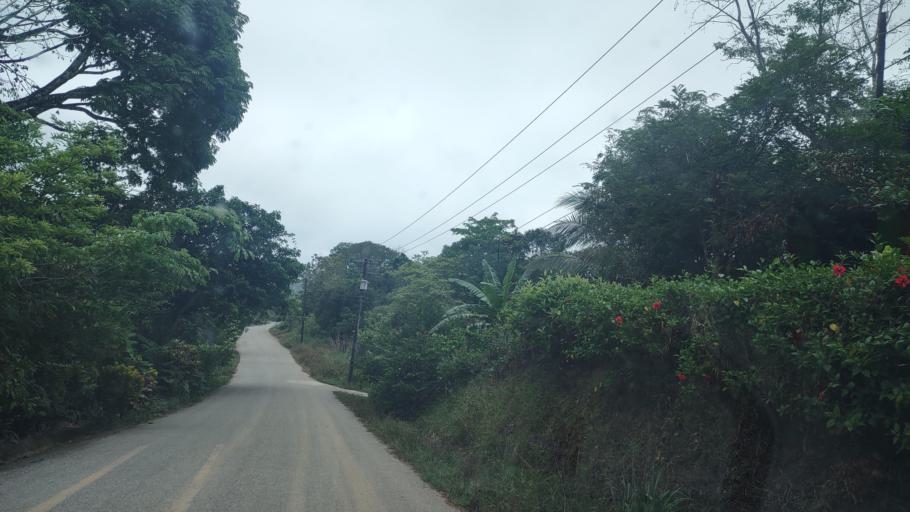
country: MX
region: Veracruz
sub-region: Uxpanapa
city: Poblado 10
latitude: 17.4764
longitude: -94.1193
